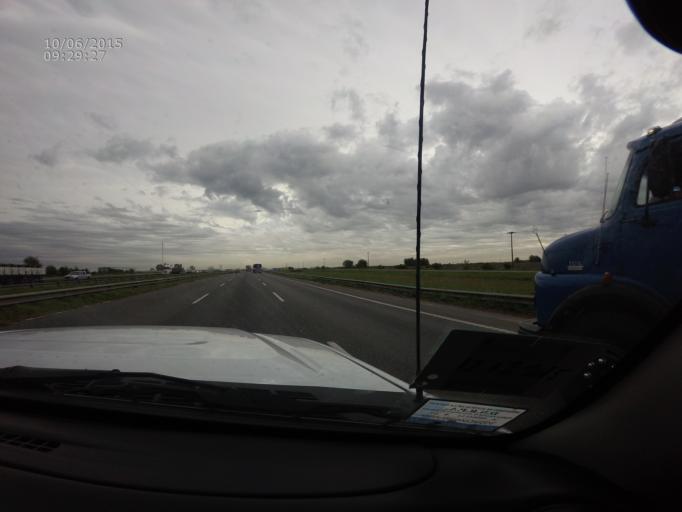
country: AR
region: Buenos Aires
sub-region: Partido de Zarate
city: Zarate
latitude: -34.1494
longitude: -59.0282
